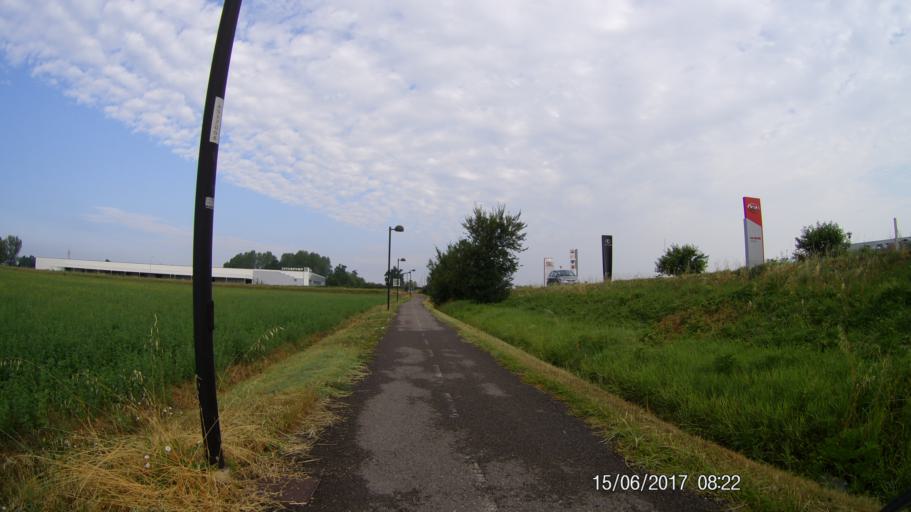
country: IT
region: Emilia-Romagna
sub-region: Provincia di Reggio Emilia
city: Roncocesi
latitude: 44.7195
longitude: 10.5703
